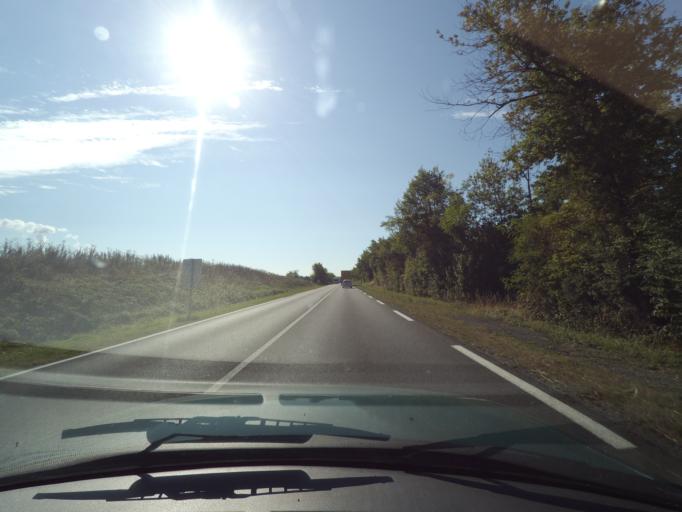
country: FR
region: Poitou-Charentes
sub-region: Departement de la Vienne
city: Terce
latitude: 46.4539
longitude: 0.5619
